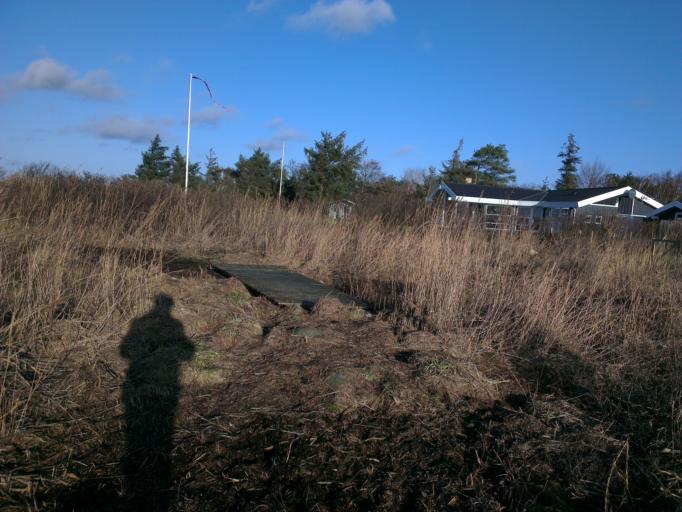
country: DK
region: Capital Region
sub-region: Frederikssund Kommune
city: Jaegerspris
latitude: 55.8395
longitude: 11.9562
